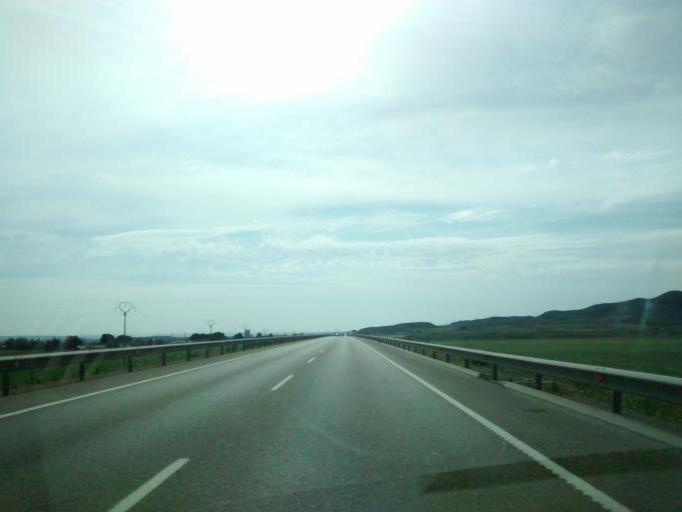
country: ES
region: Aragon
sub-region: Provincia de Zaragoza
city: El Burgo de Ebro
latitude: 41.5550
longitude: -0.7189
